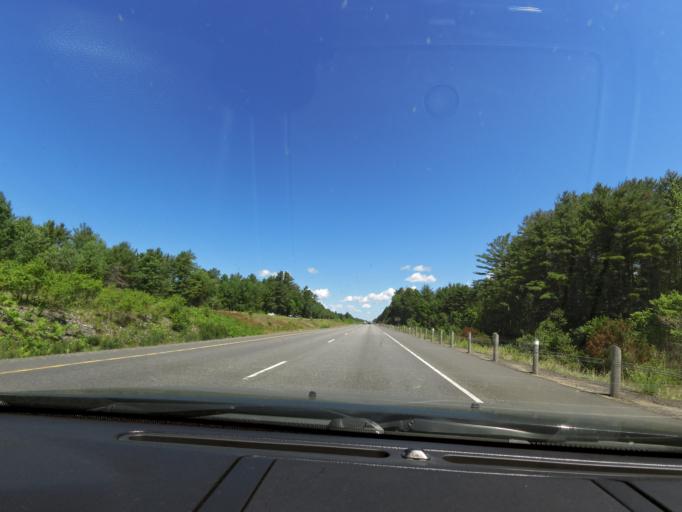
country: CA
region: Ontario
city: Bracebridge
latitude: 45.1192
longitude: -79.3106
